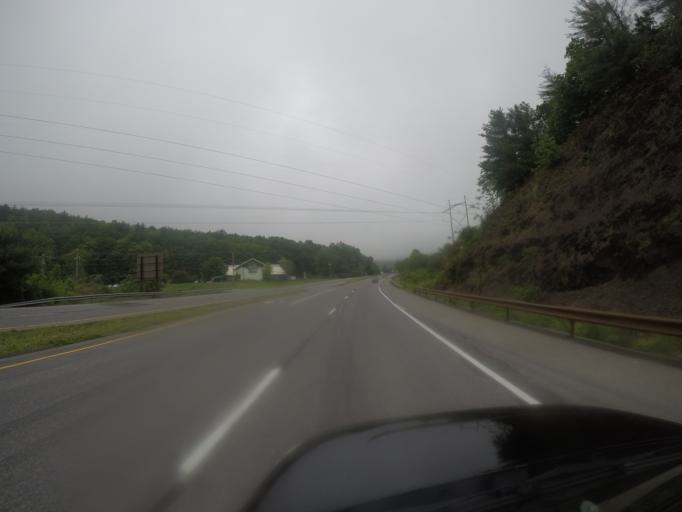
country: US
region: New York
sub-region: Ulster County
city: Hurley
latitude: 41.9524
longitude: -74.0475
